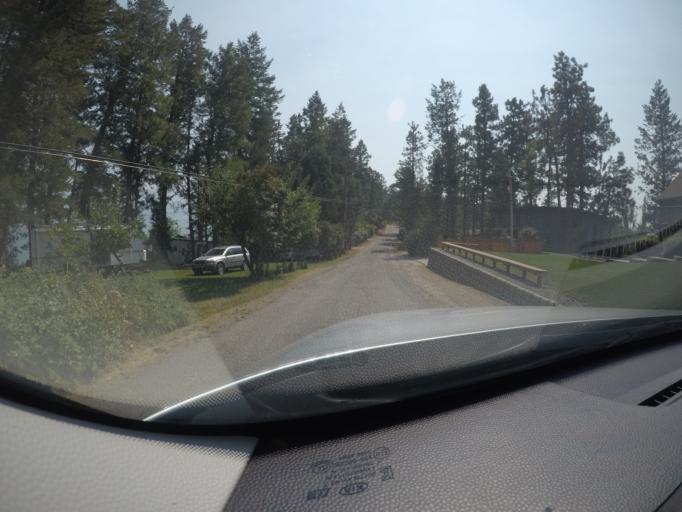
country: US
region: Montana
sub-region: Lake County
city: Polson
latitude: 47.7657
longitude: -114.1421
